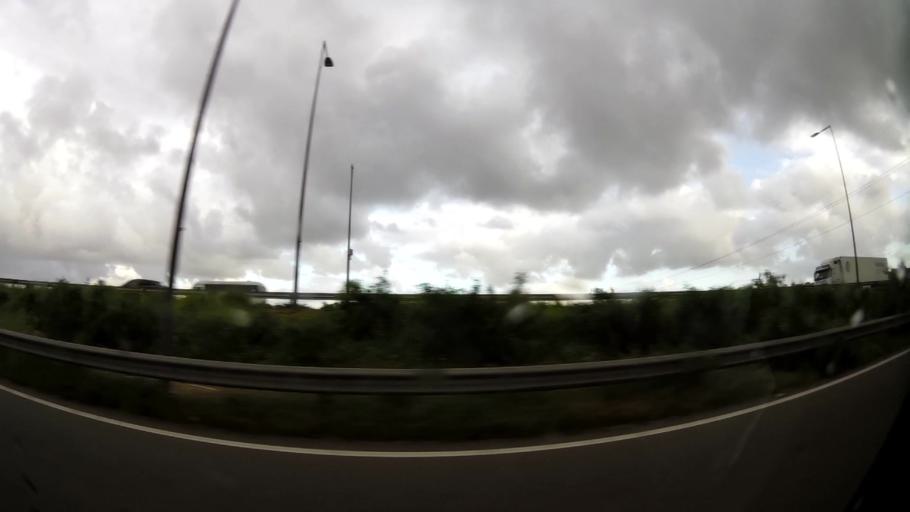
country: MA
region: Grand Casablanca
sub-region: Mohammedia
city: Mohammedia
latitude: 33.6545
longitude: -7.4130
